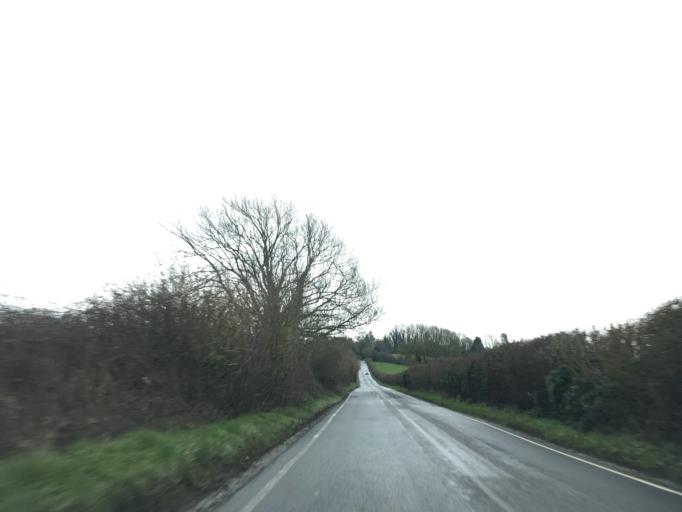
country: GB
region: England
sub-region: Borough of Swindon
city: Wanborough
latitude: 51.5433
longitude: -1.7124
